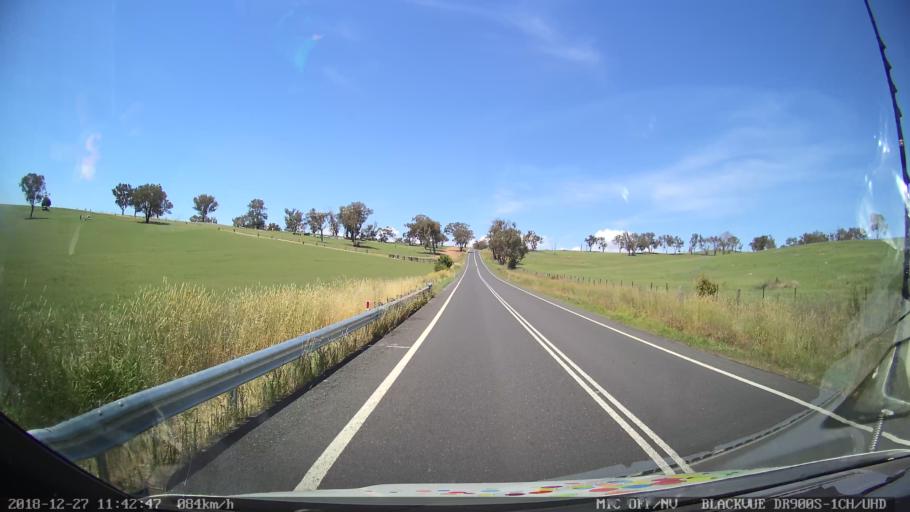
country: AU
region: New South Wales
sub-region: Bathurst Regional
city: Perthville
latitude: -33.5526
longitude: 149.4774
